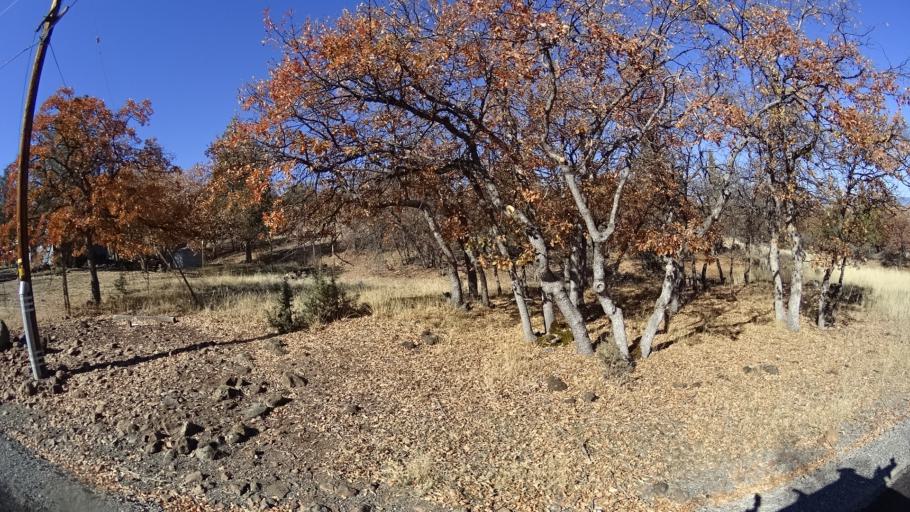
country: US
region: California
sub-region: Siskiyou County
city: Montague
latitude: 41.8799
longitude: -122.4864
